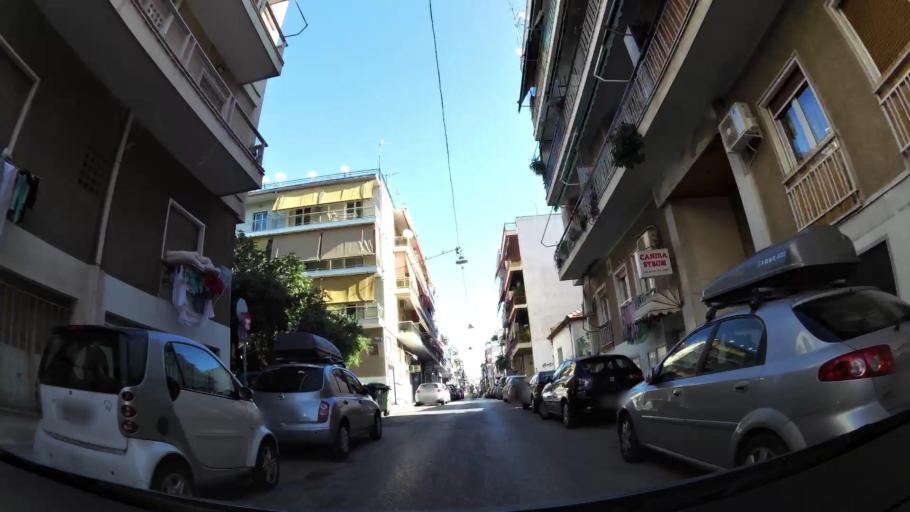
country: GR
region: Attica
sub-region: Nomarchia Athinas
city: Neo Psychiko
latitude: 37.9951
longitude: 23.7719
